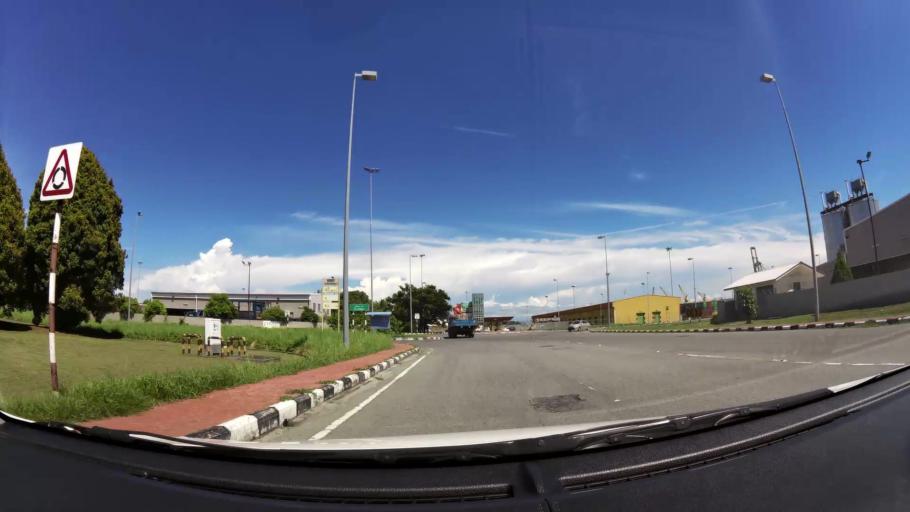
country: BN
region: Brunei and Muara
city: Bandar Seri Begawan
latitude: 5.0292
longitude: 115.0714
